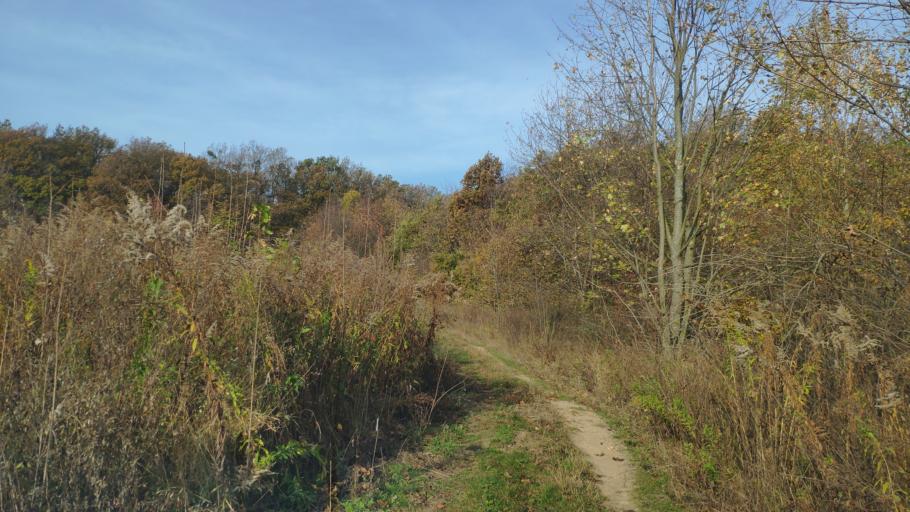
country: SK
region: Kosicky
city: Kosice
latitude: 48.7468
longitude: 21.2211
